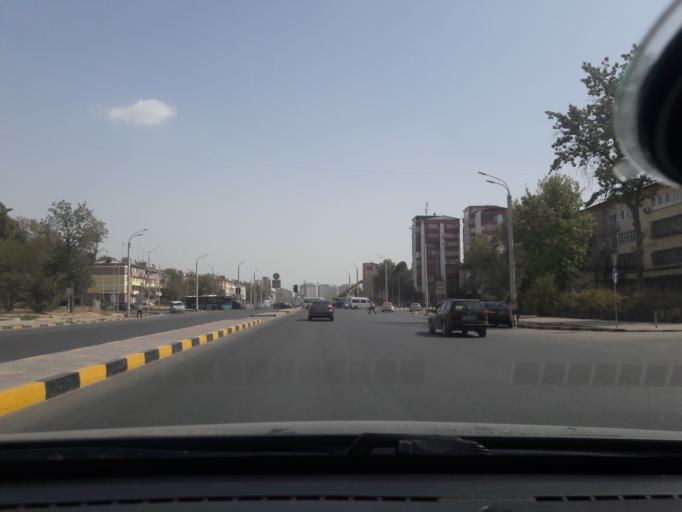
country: TJ
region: Dushanbe
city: Dushanbe
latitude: 38.5584
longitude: 68.7466
